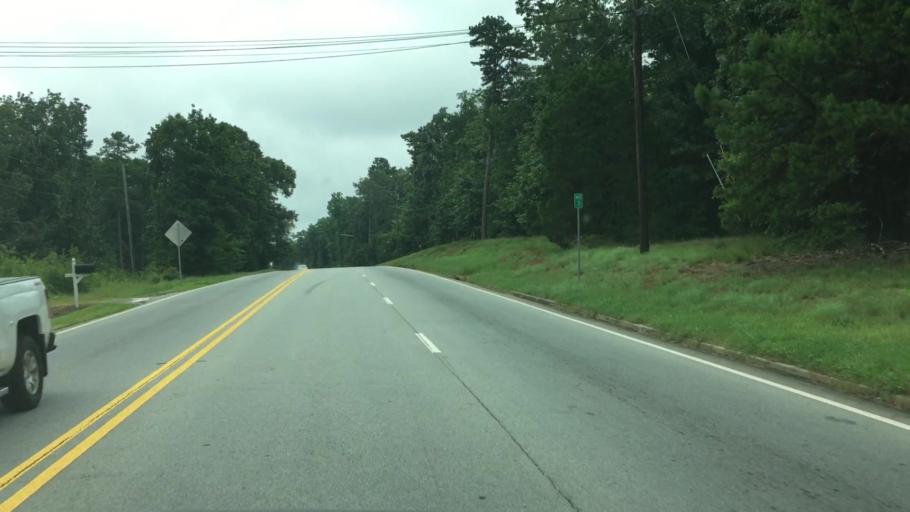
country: US
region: Georgia
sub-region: Barrow County
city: Winder
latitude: 34.0136
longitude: -83.7074
